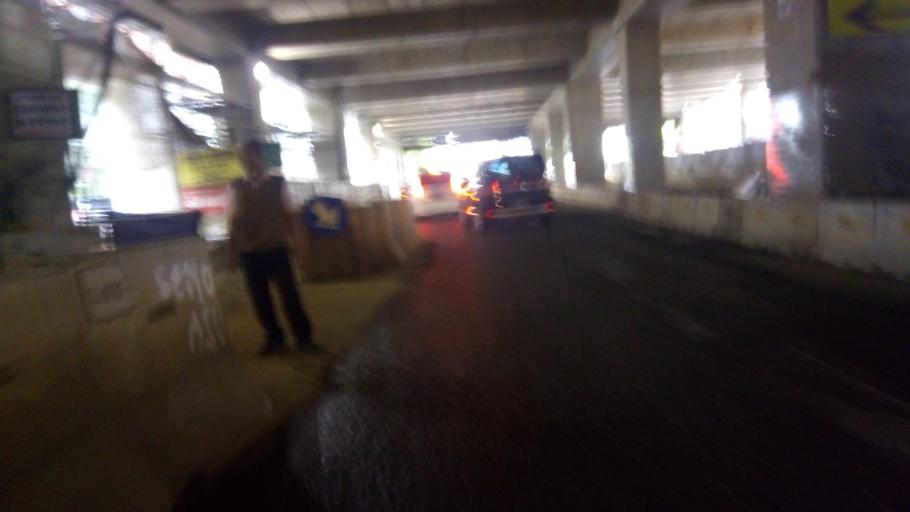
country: ID
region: Jakarta Raya
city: Jakarta
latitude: -6.2445
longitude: 106.7982
